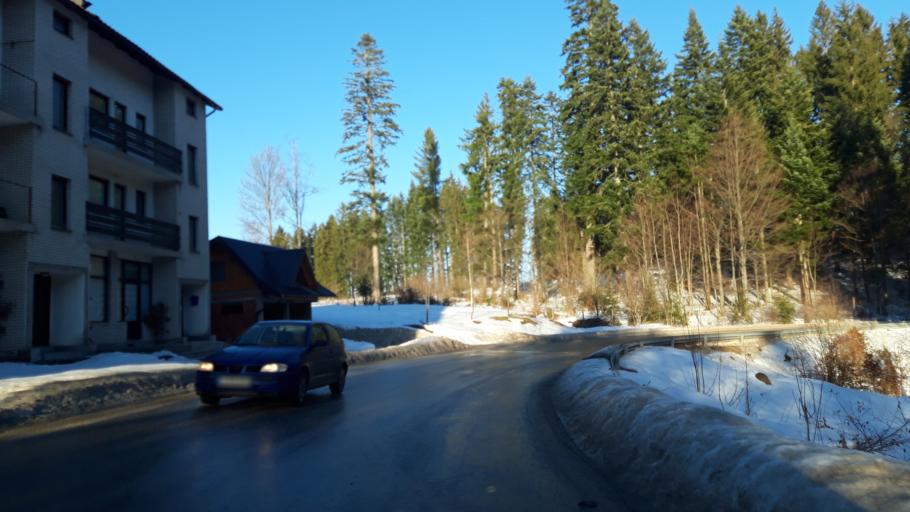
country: BA
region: Republika Srpska
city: Han Pijesak
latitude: 44.0767
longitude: 18.9509
